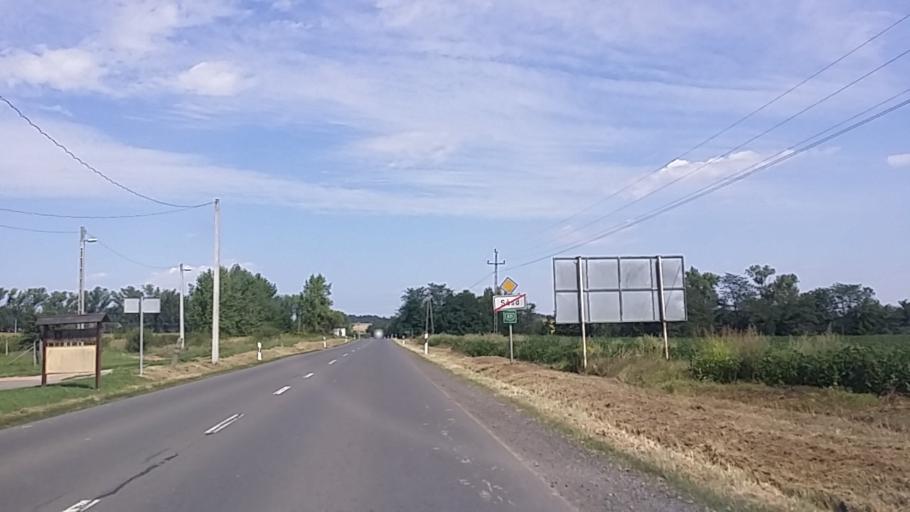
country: HU
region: Baranya
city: Sasd
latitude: 46.2653
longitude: 18.1045
